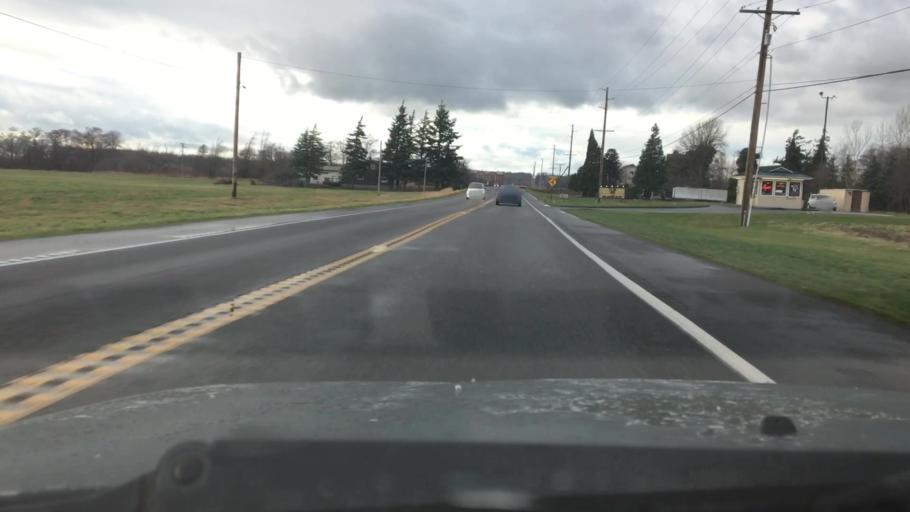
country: US
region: Washington
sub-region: Whatcom County
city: Ferndale
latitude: 48.8192
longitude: -122.6087
